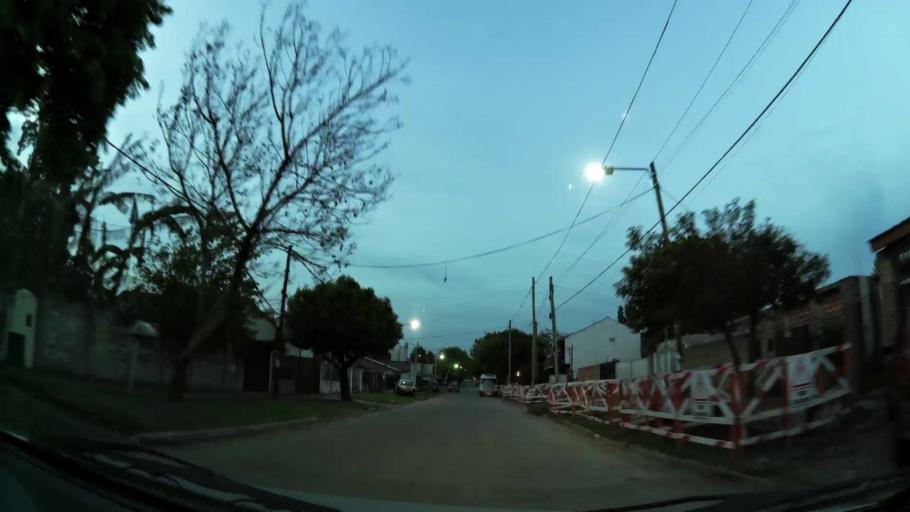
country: AR
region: Buenos Aires
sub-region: Partido de Quilmes
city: Quilmes
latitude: -34.8050
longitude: -58.2851
